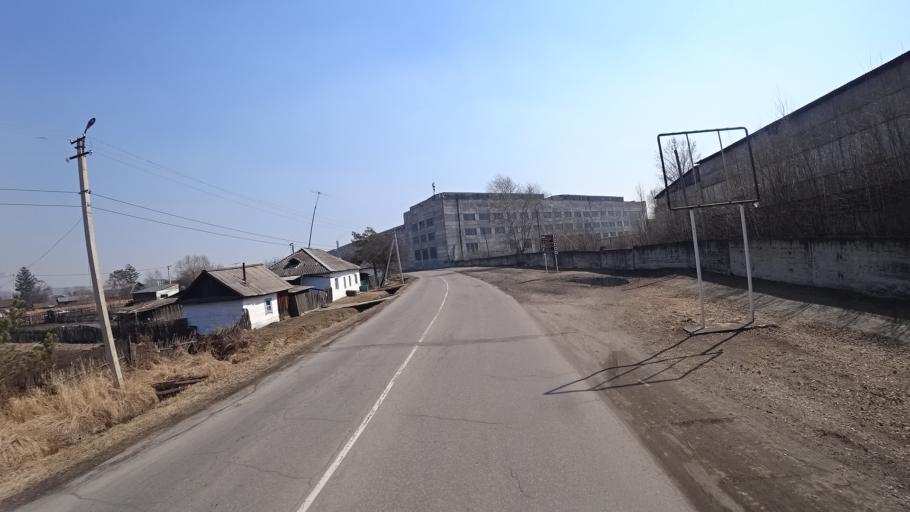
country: RU
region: Amur
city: Novobureyskiy
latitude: 49.7928
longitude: 129.8567
